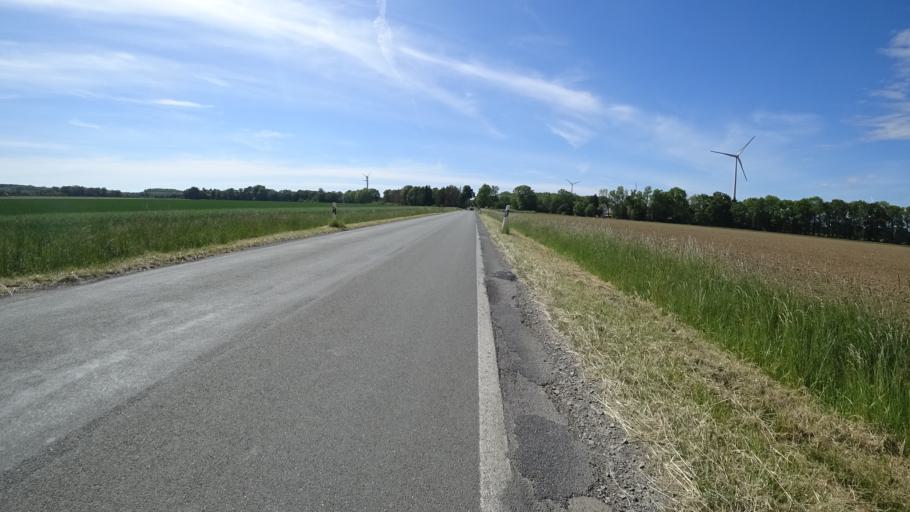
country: DE
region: North Rhine-Westphalia
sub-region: Regierungsbezirk Detmold
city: Rheda-Wiedenbruck
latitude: 51.8228
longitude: 8.2465
